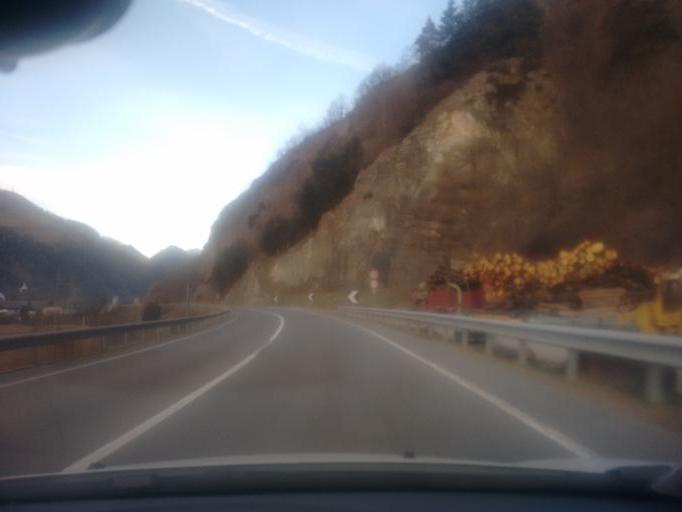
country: IT
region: Trentino-Alto Adige
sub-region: Bolzano
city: Prati
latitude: 46.8823
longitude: 11.4570
